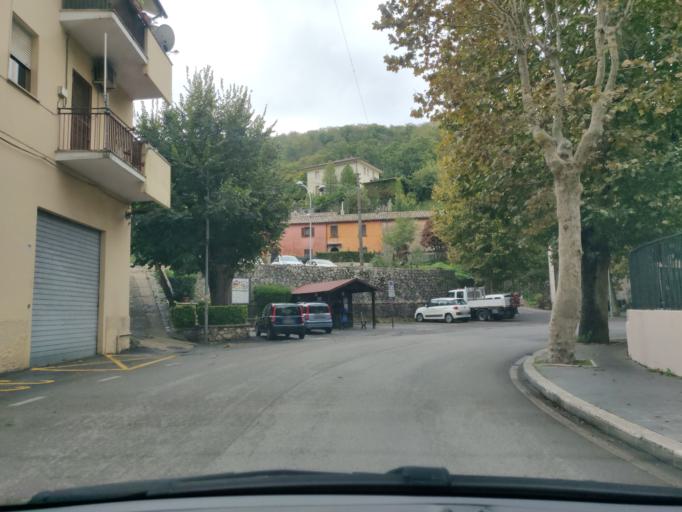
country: IT
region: Latium
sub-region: Citta metropolitana di Roma Capitale
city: Allumiere
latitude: 42.1540
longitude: 11.9055
